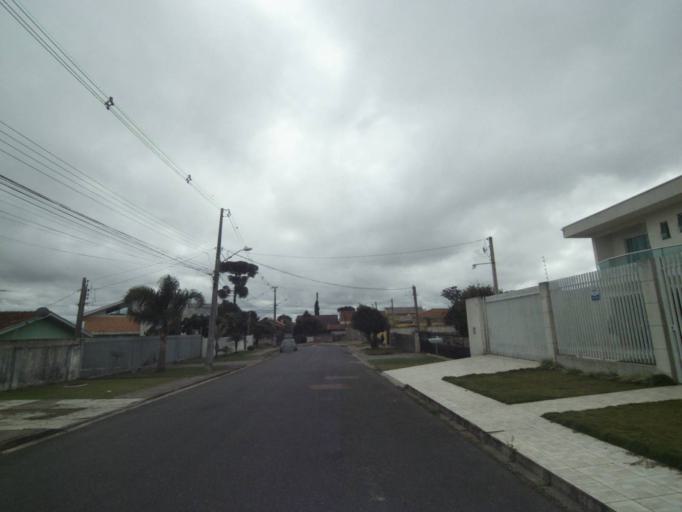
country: BR
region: Parana
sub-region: Sao Jose Dos Pinhais
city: Sao Jose dos Pinhais
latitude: -25.5375
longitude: -49.2976
